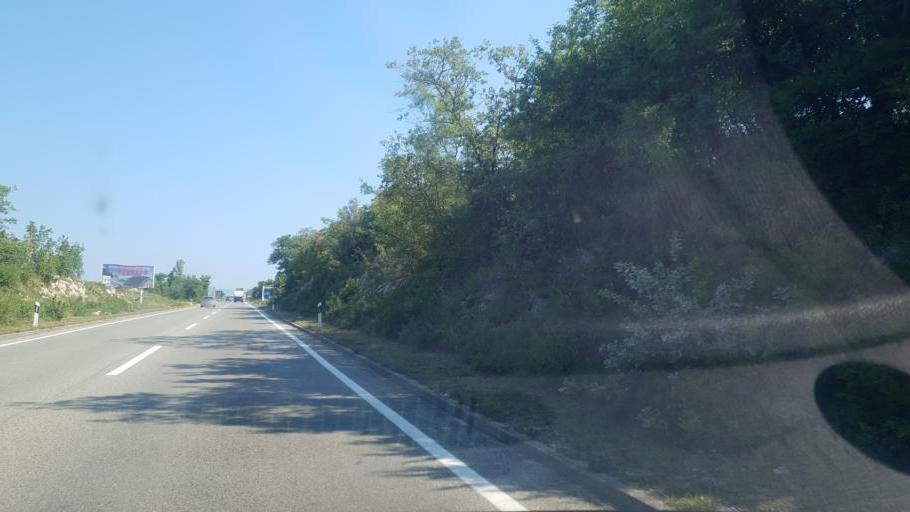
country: HR
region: Primorsko-Goranska
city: Omisalj
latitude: 45.2088
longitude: 14.5669
